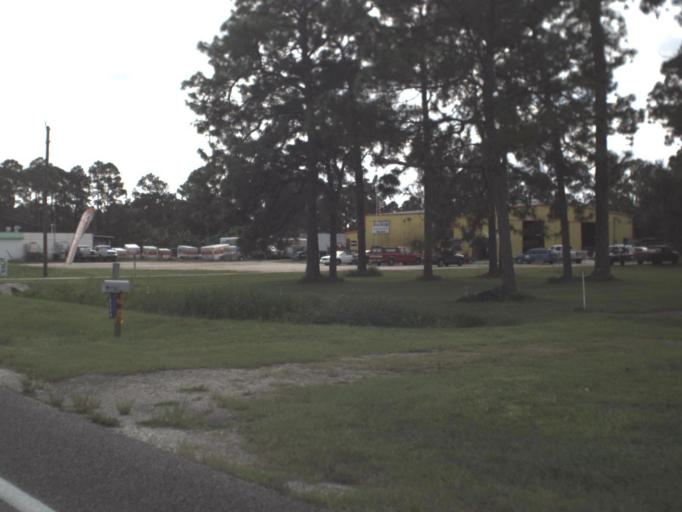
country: US
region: Florida
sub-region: Lee County
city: Alva
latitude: 26.7132
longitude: -81.6577
